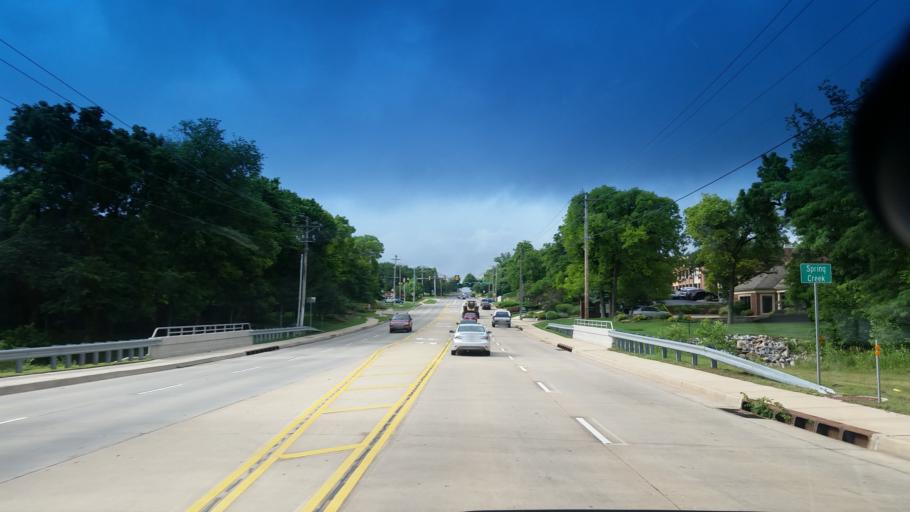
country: US
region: Oklahoma
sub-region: Oklahoma County
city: Edmond
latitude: 35.6402
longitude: -97.4605
